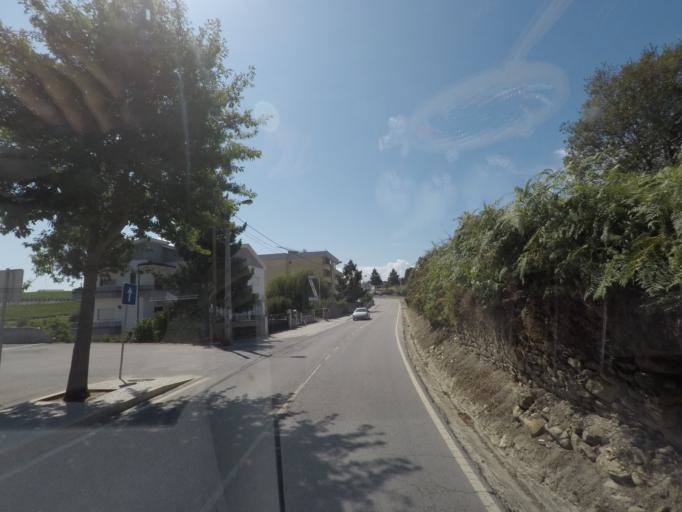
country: PT
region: Vila Real
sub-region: Sabrosa
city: Sabrosa
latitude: 41.2694
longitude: -7.4785
